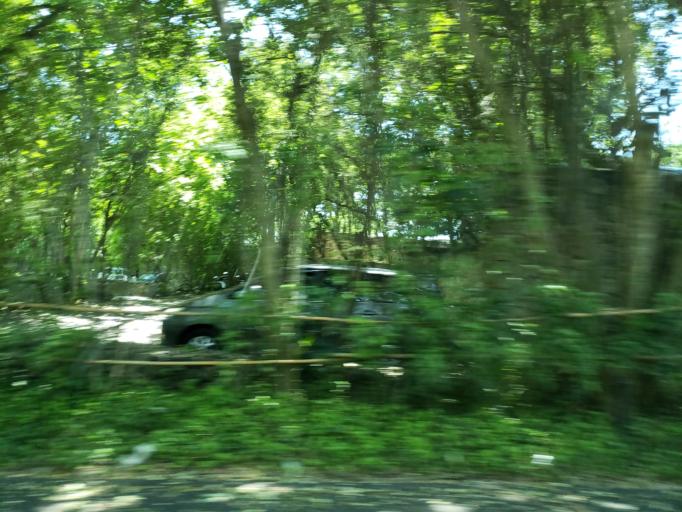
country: ID
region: Bali
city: Kangin
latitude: -8.8456
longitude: 115.1377
